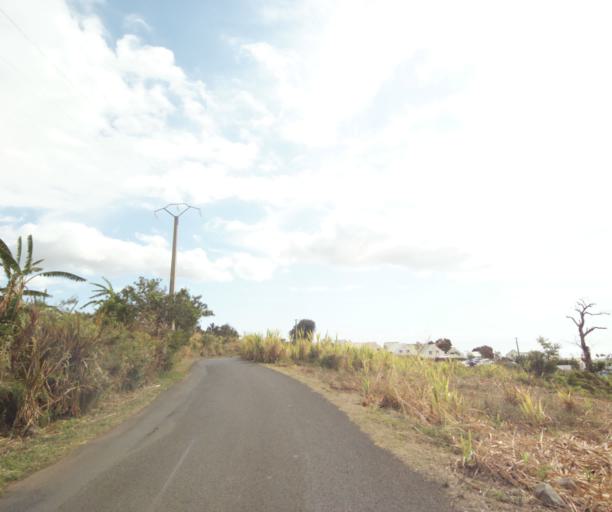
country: RE
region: Reunion
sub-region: Reunion
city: Saint-Paul
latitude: -21.0293
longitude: 55.2877
